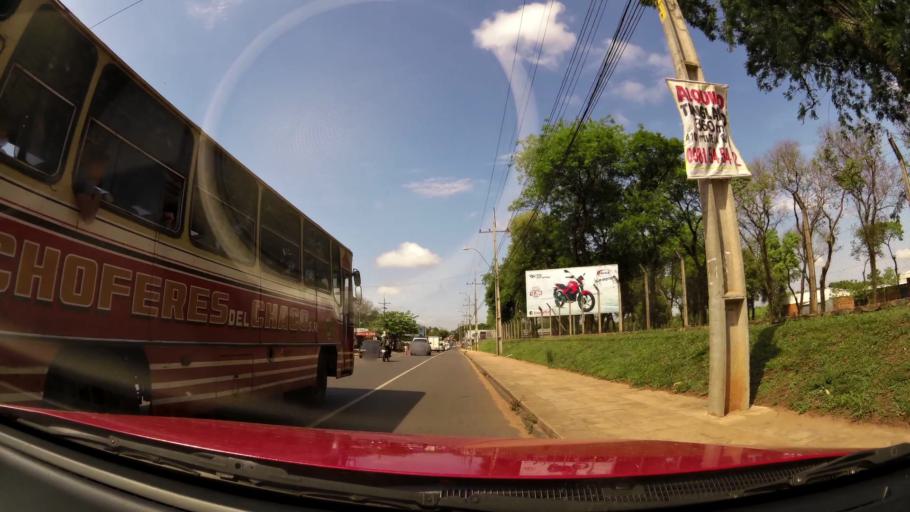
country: PY
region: Central
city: San Lorenzo
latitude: -25.2975
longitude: -57.5029
